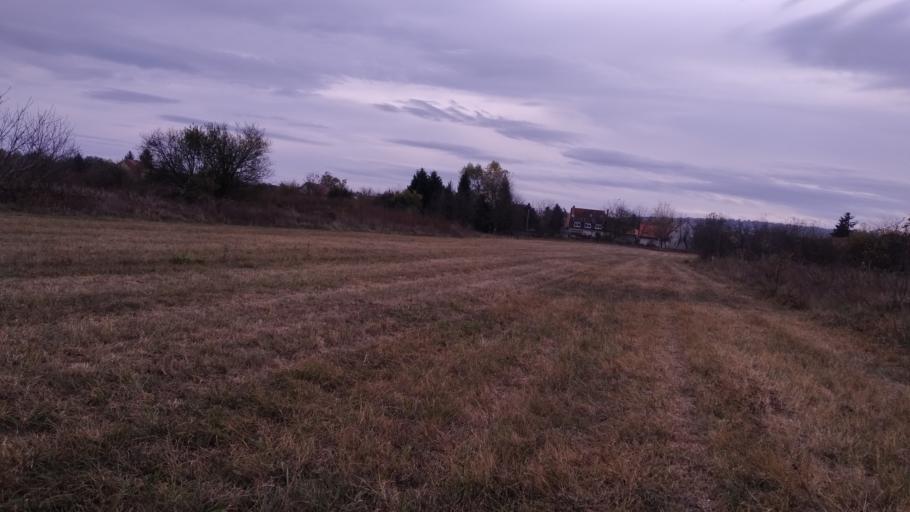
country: HU
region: Pest
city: Budakalasz
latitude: 47.6335
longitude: 19.0450
